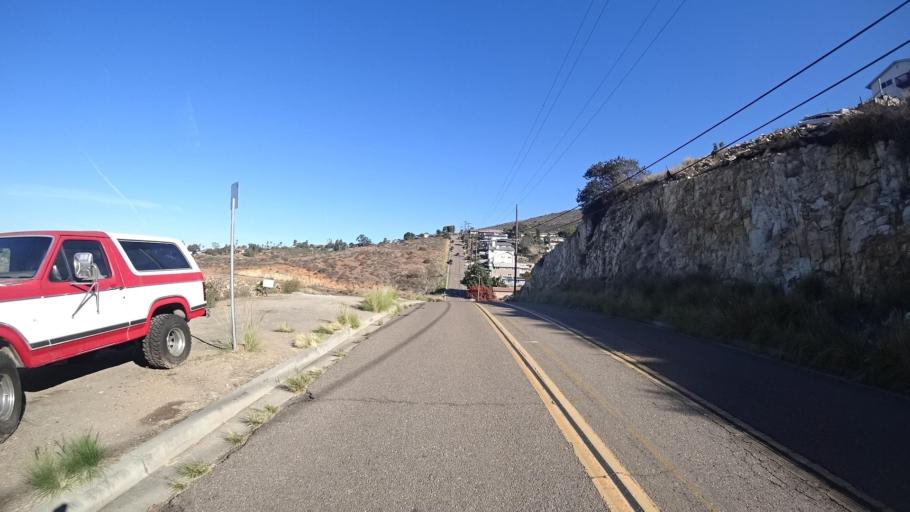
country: US
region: California
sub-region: San Diego County
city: La Presa
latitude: 32.7192
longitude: -116.9972
